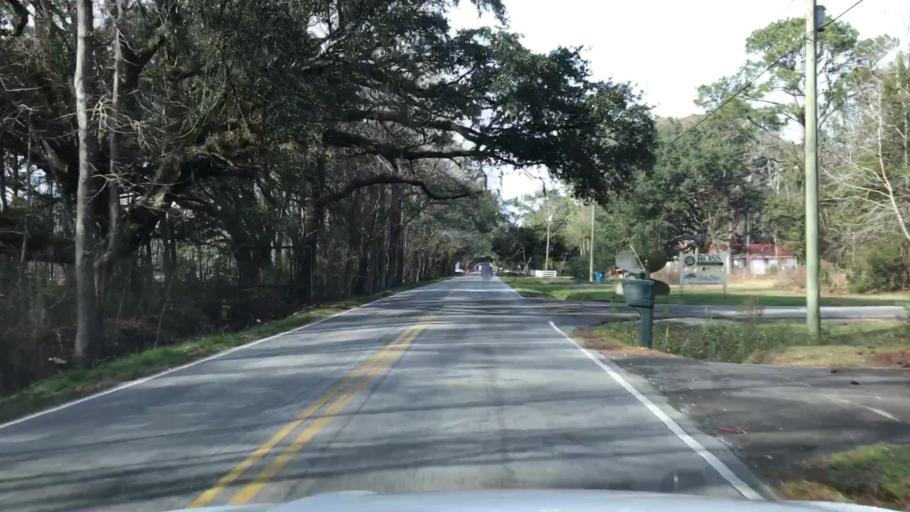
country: US
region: South Carolina
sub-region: Charleston County
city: Shell Point
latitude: 32.7651
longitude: -80.0645
